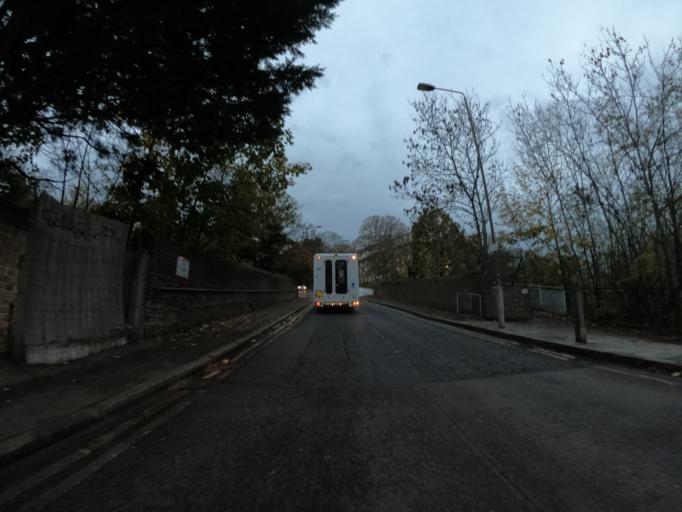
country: GB
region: England
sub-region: Greater London
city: Blackheath
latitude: 51.4833
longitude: 0.0085
